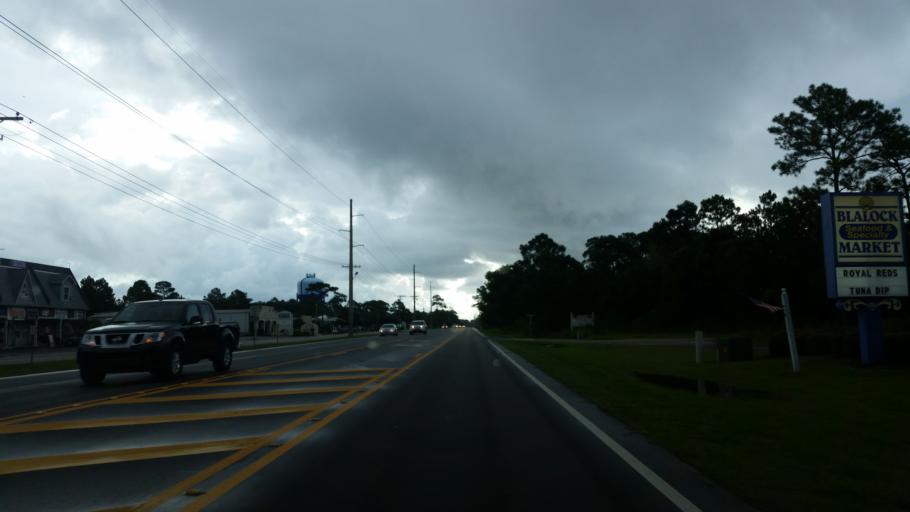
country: US
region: Alabama
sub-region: Baldwin County
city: Orange Beach
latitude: 30.2903
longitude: -87.6023
